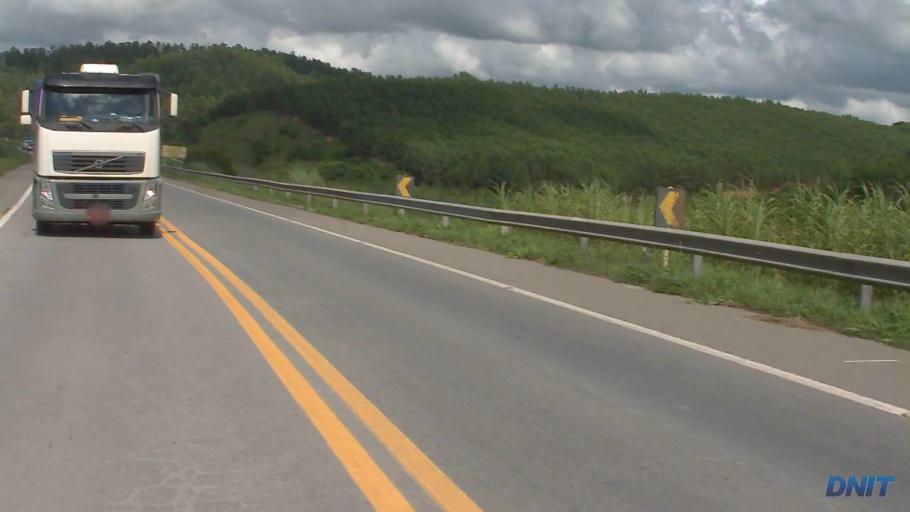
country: BR
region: Minas Gerais
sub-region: Governador Valadares
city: Governador Valadares
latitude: -19.0723
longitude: -42.1768
